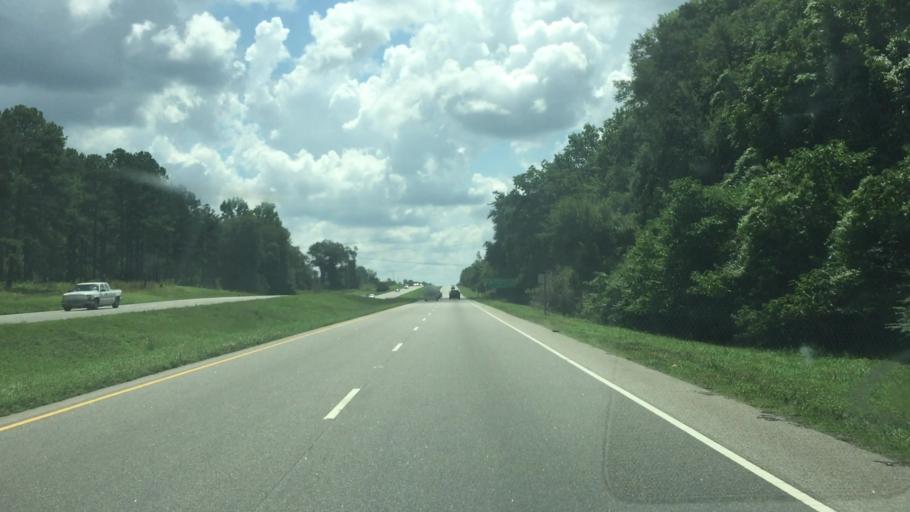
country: US
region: North Carolina
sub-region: Richmond County
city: Hamlet
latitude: 34.8547
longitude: -79.6237
